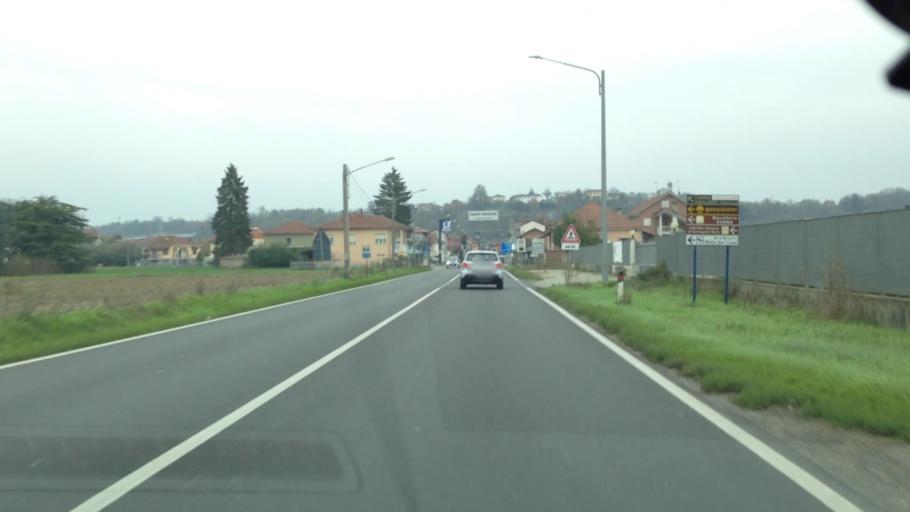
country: IT
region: Piedmont
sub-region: Provincia di Asti
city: Azzano d'Asti
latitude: 44.9073
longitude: 8.2784
